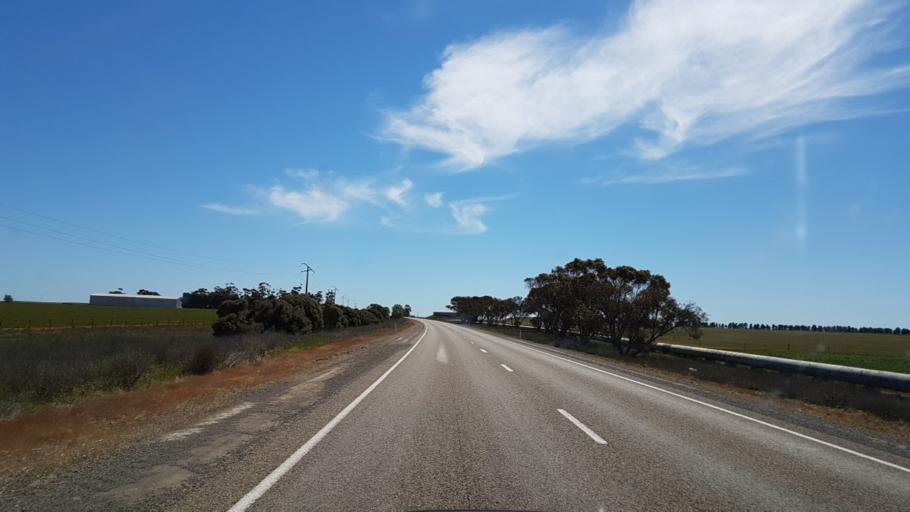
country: AU
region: South Australia
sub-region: Clare and Gilbert Valleys
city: Clare
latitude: -33.7906
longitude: 138.8464
